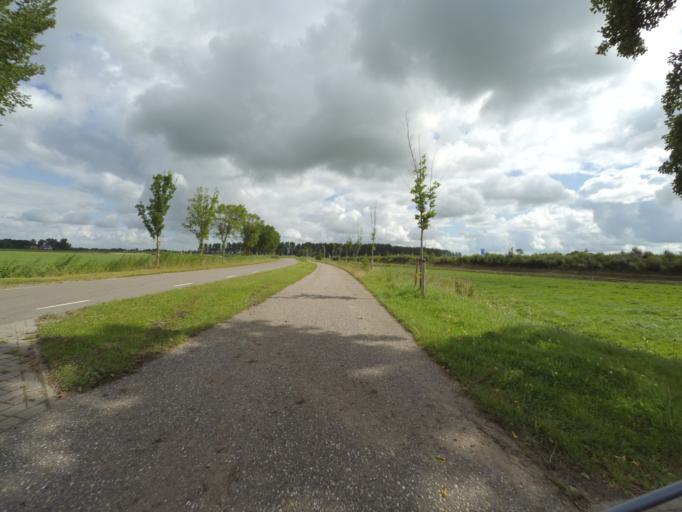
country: NL
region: Friesland
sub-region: Gemeente Achtkarspelen
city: Buitenpost
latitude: 53.2580
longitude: 6.1644
